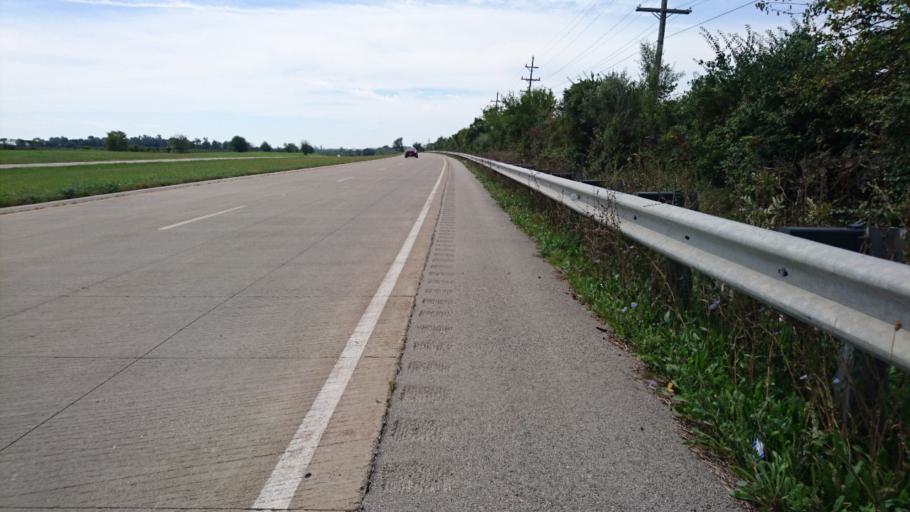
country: US
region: Illinois
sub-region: Will County
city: Elwood
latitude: 41.3737
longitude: -88.1314
